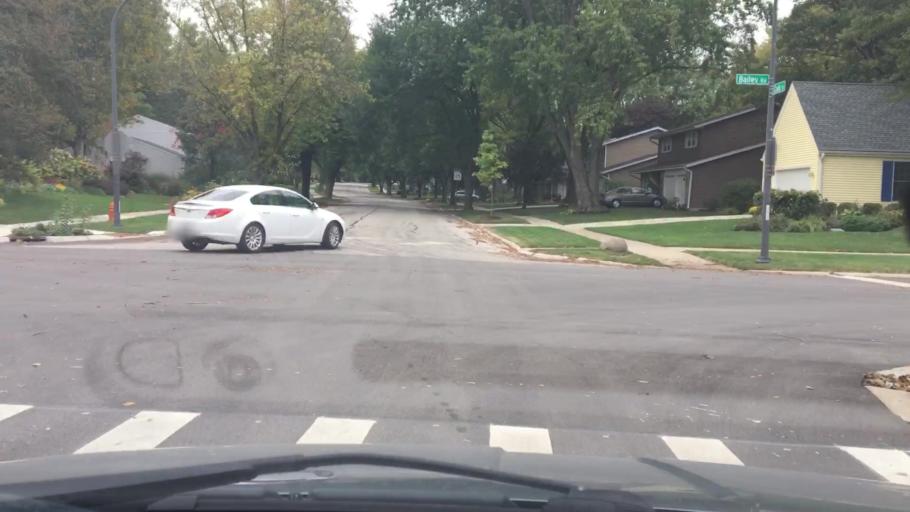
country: US
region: Illinois
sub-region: DuPage County
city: Naperville
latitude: 41.7412
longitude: -88.1352
